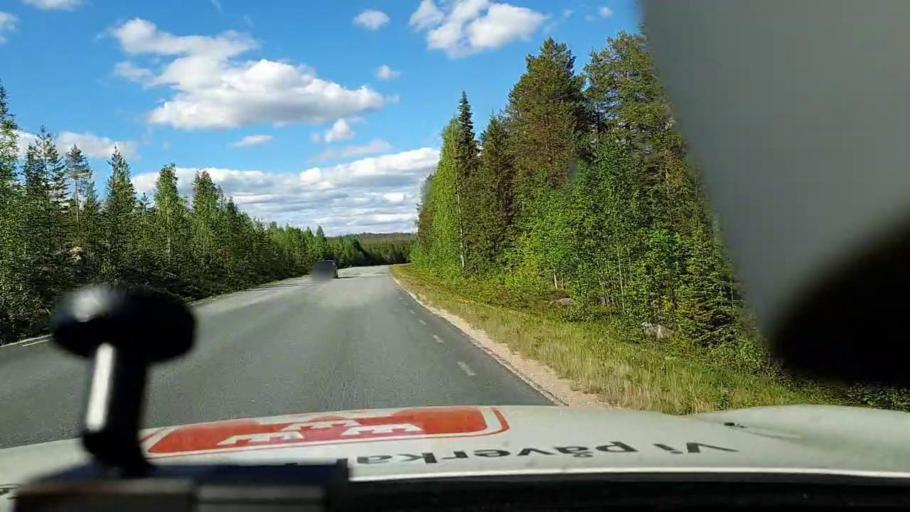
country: FI
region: Lapland
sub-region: Torniolaakso
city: Ylitornio
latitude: 66.3179
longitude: 23.6200
